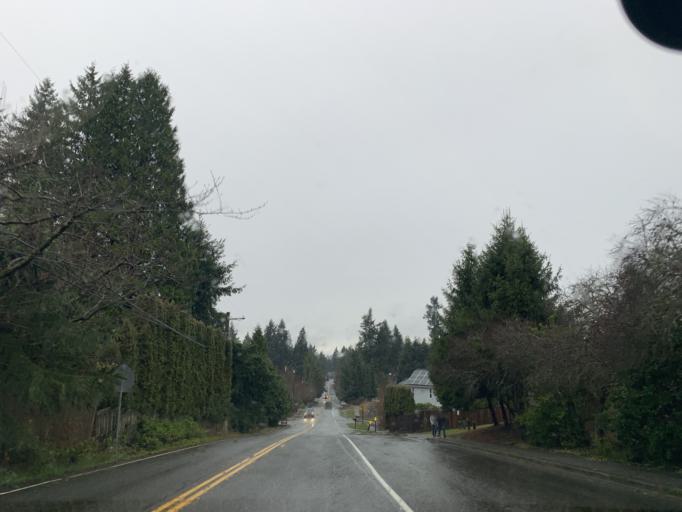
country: US
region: Washington
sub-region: King County
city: Kingsgate
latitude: 47.7258
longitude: -122.1691
